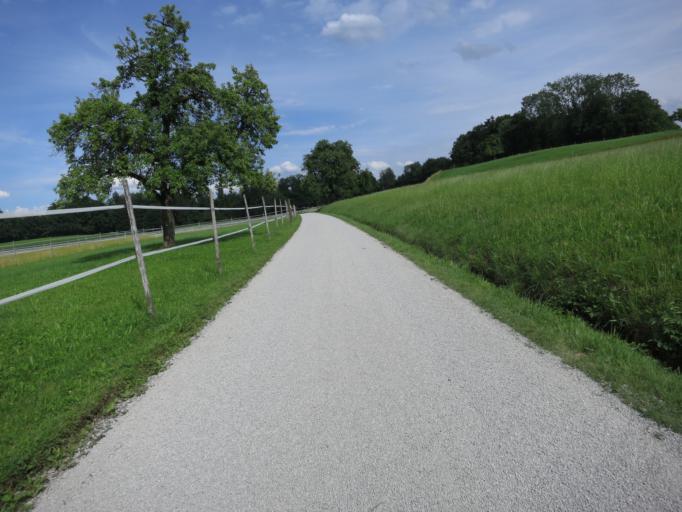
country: CH
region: Zurich
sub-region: Bezirk Hinwil
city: Wolfhausen
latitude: 47.2498
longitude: 8.8014
